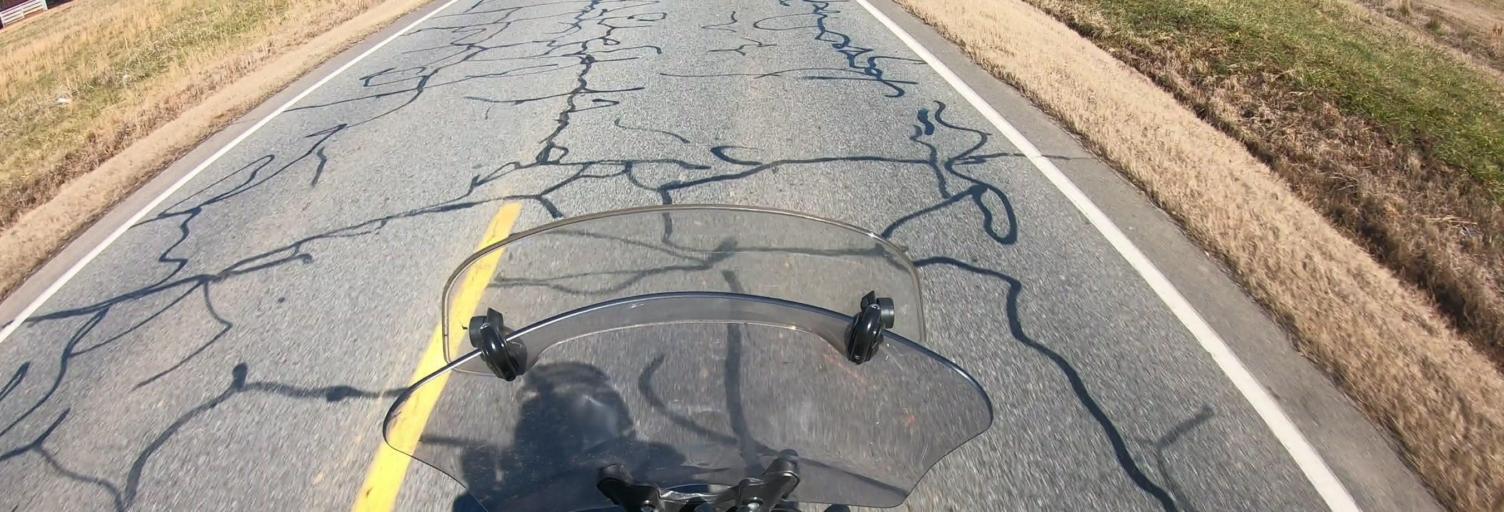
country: US
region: Georgia
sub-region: Murray County
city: Chatsworth
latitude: 34.5728
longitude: -84.7048
